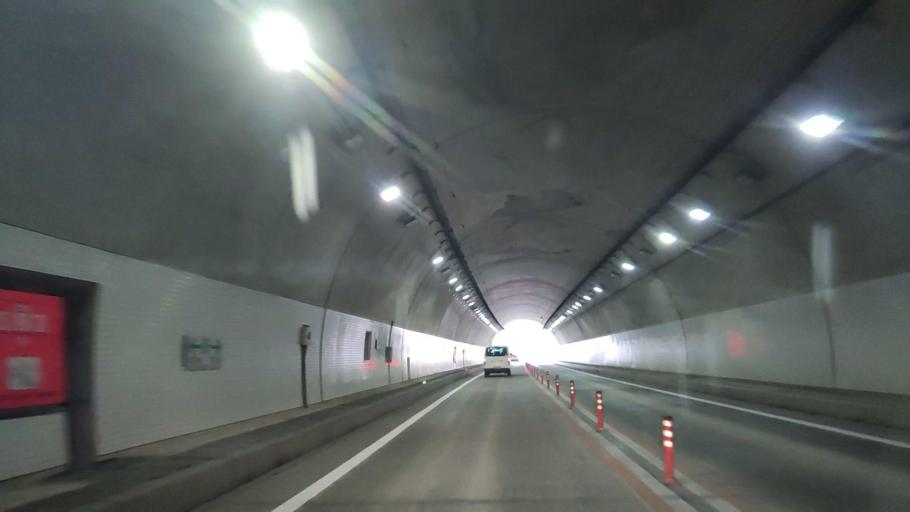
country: JP
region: Akita
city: Odate
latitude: 40.3292
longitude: 140.6074
